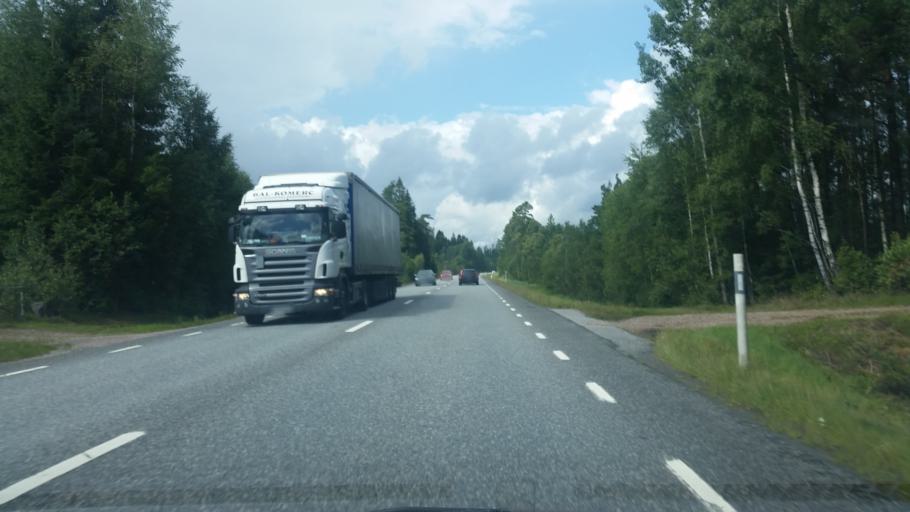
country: SE
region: Vaestra Goetaland
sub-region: Tranemo Kommun
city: Langhem
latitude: 57.5911
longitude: 13.1995
